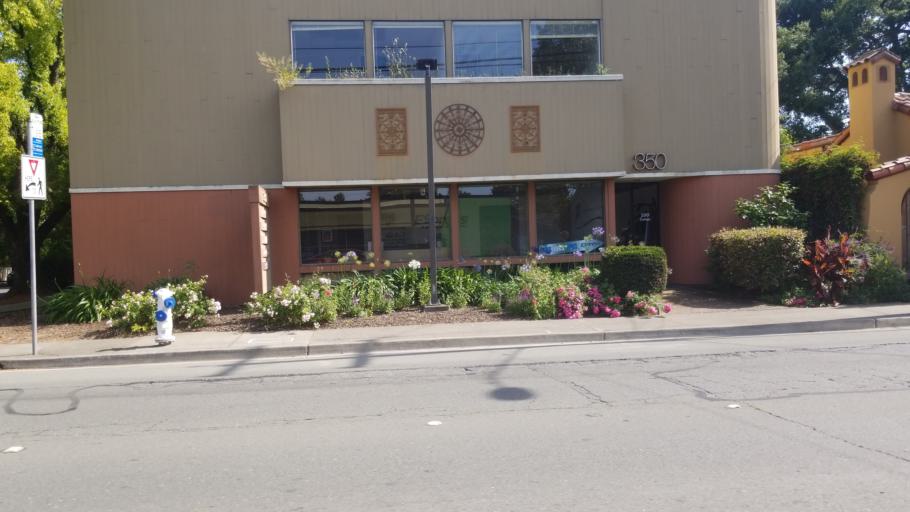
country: US
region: California
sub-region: Sonoma County
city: Santa Rosa
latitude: 38.4457
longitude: -122.7206
